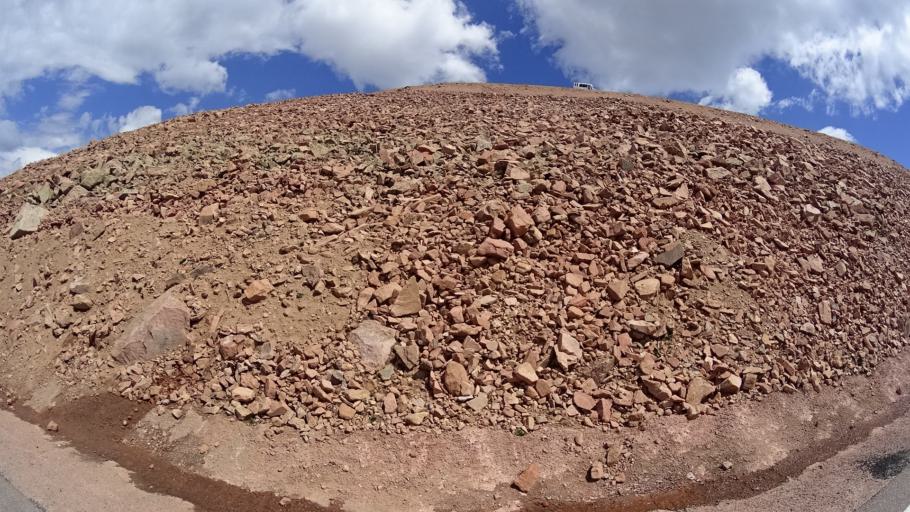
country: US
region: Colorado
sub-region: El Paso County
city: Cascade-Chipita Park
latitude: 38.8378
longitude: -105.0466
